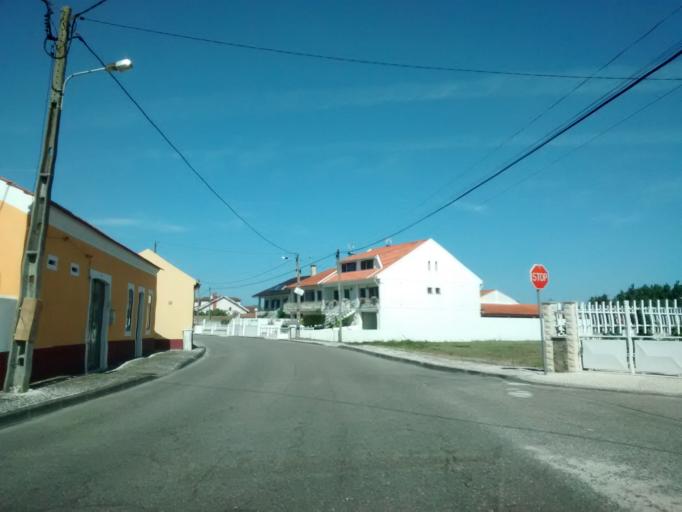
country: PT
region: Coimbra
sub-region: Mira
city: Mira
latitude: 40.4282
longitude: -8.6852
